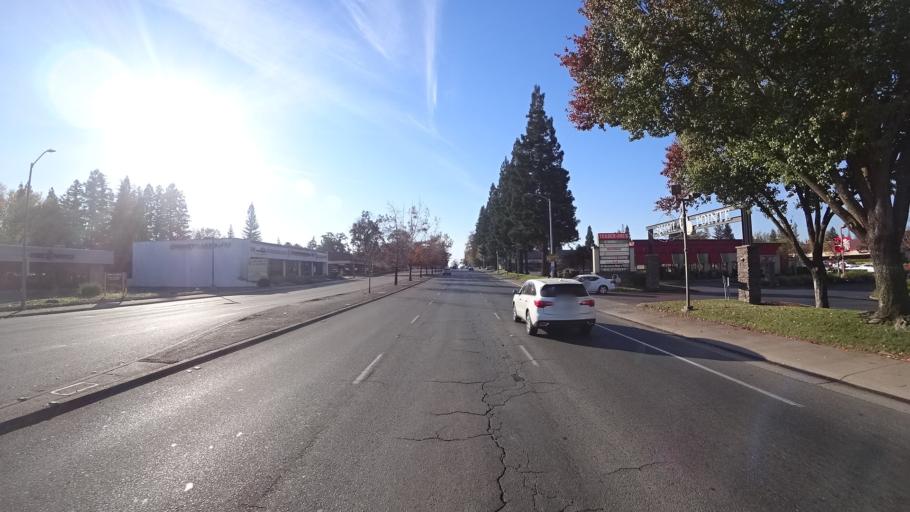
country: US
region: California
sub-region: Sacramento County
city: Fair Oaks
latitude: 38.6630
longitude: -121.2723
